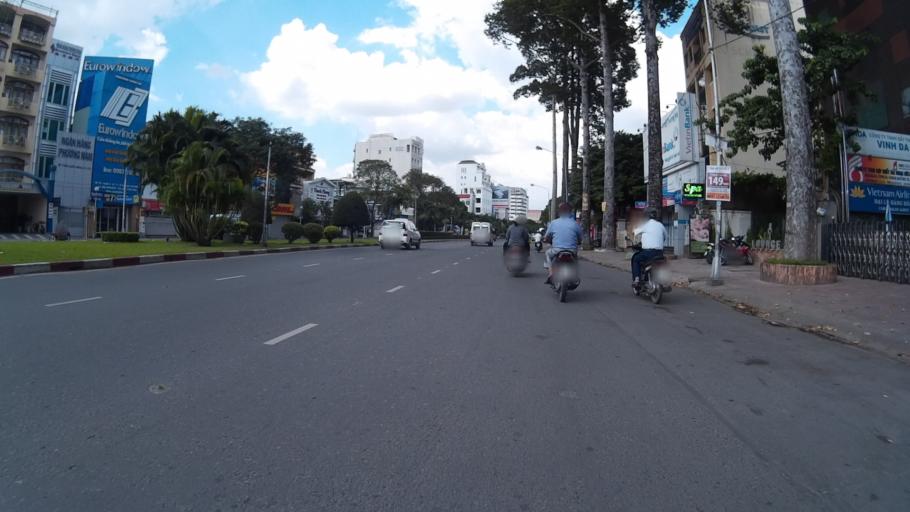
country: VN
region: Ho Chi Minh City
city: Quan Phu Nhuan
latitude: 10.8050
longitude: 106.6647
